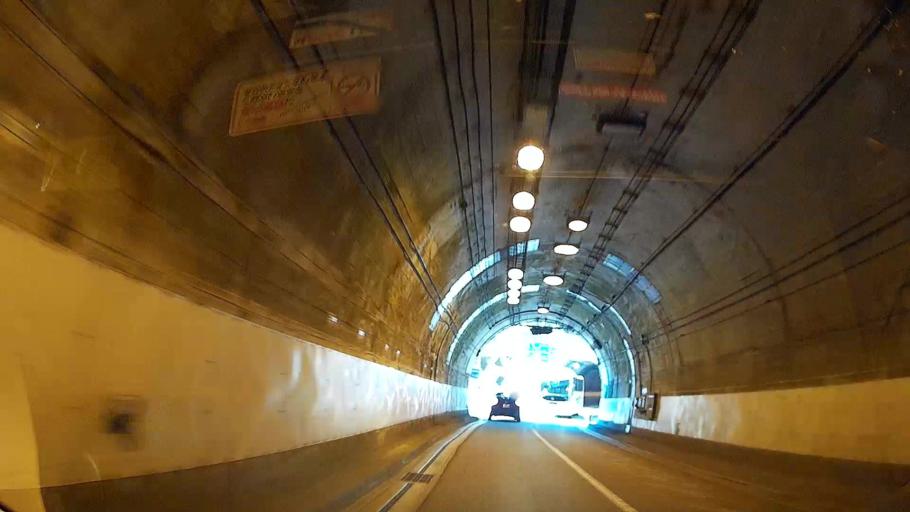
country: JP
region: Nagano
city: Toyoshina
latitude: 36.1517
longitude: 137.6843
